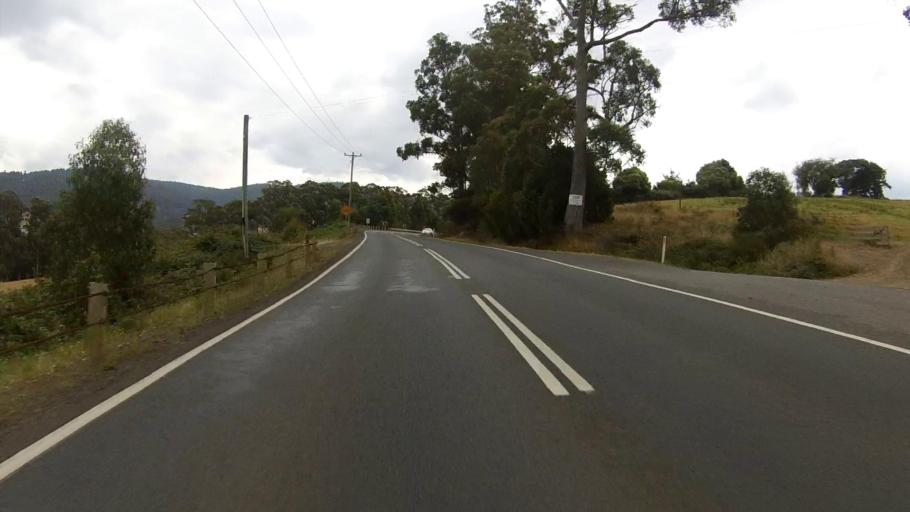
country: AU
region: Tasmania
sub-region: Huon Valley
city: Huonville
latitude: -43.0643
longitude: 147.0411
